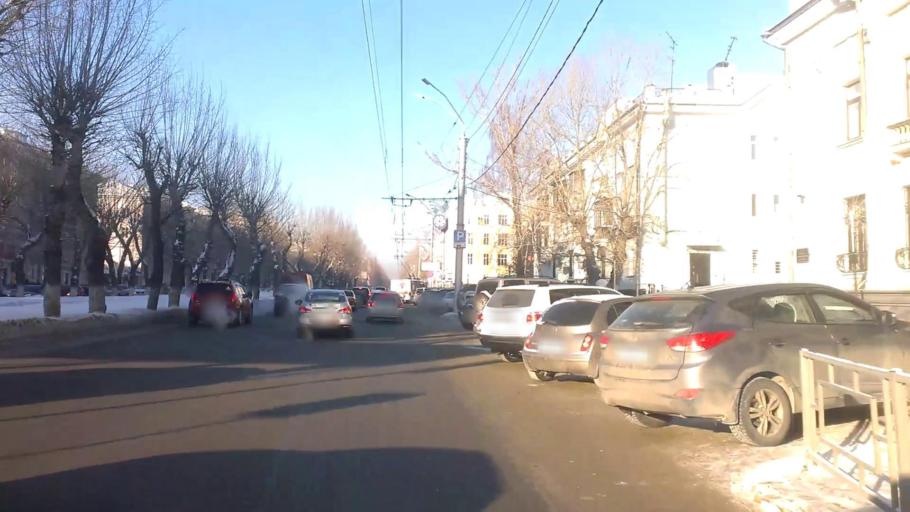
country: RU
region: Altai Krai
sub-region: Gorod Barnaulskiy
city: Barnaul
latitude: 53.3490
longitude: 83.7763
